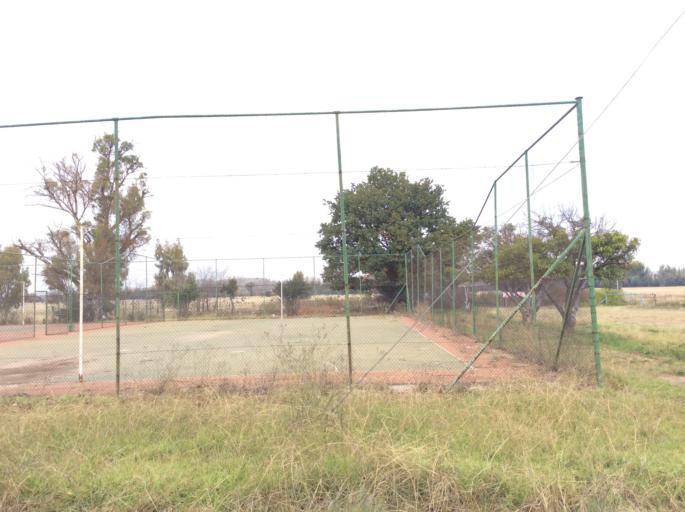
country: LS
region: Mafeteng
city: Mafeteng
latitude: -29.7316
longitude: 27.0410
